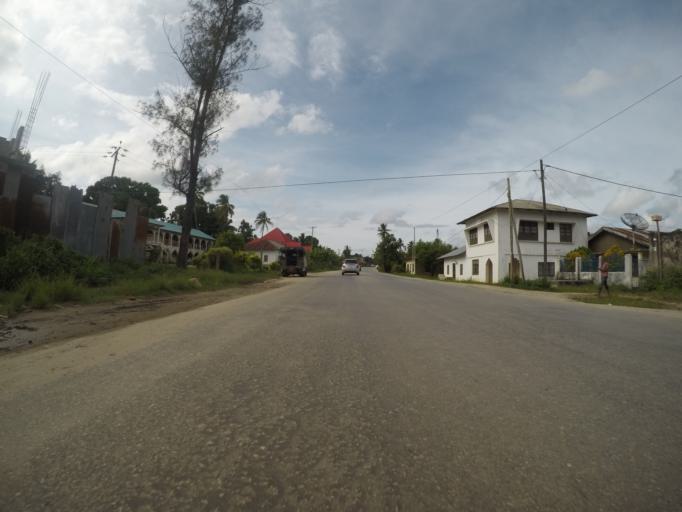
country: TZ
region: Pemba South
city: Chake Chake
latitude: -5.2318
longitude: 39.7761
